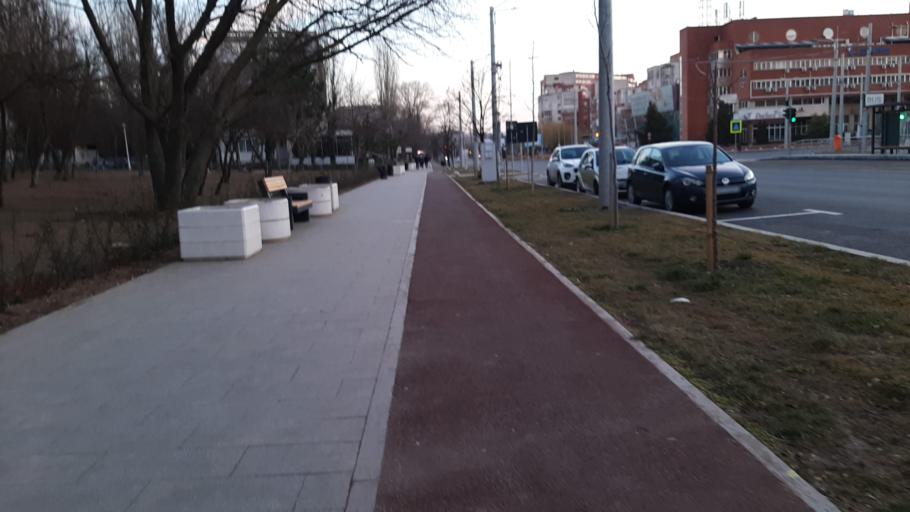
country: RO
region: Galati
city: Galati
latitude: 45.4314
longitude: 28.0253
